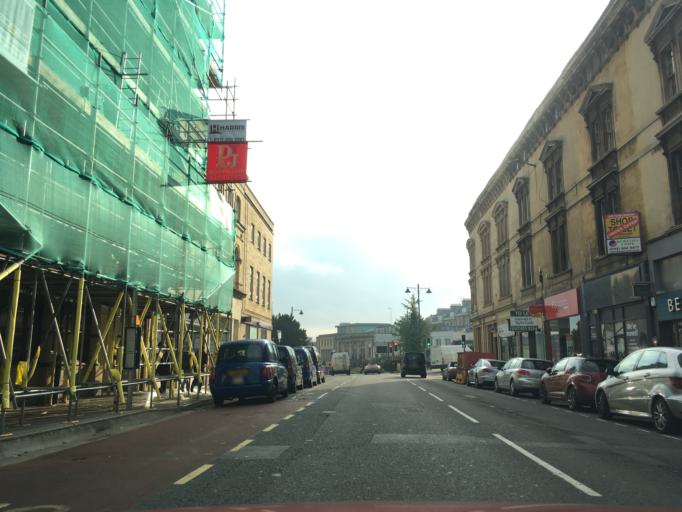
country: GB
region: England
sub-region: Bristol
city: Bristol
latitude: 51.4566
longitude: -2.6068
